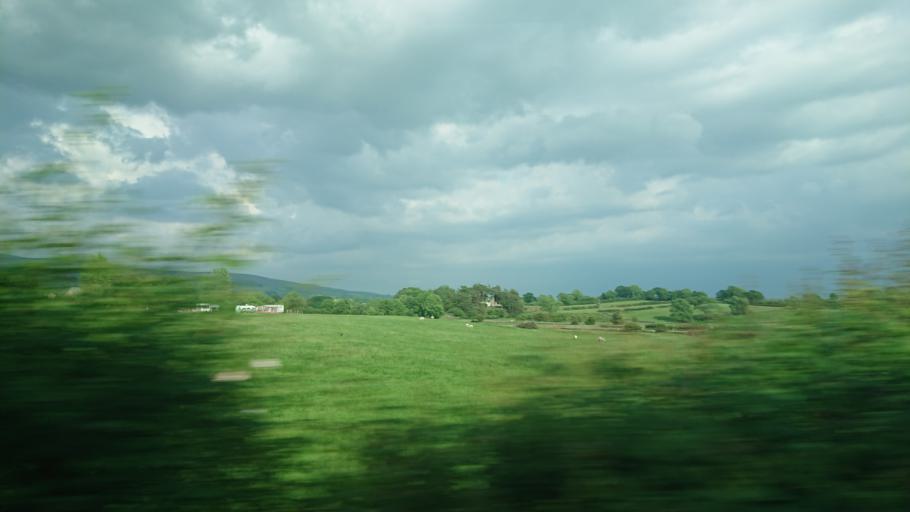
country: GB
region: England
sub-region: North Yorkshire
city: Ingleton
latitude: 54.1454
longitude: -2.4954
